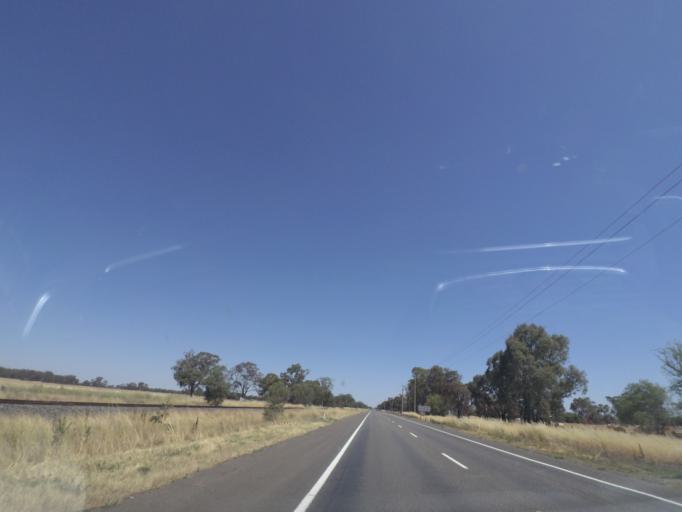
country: AU
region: Victoria
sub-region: Greater Shepparton
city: Shepparton
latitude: -36.2425
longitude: 145.4319
